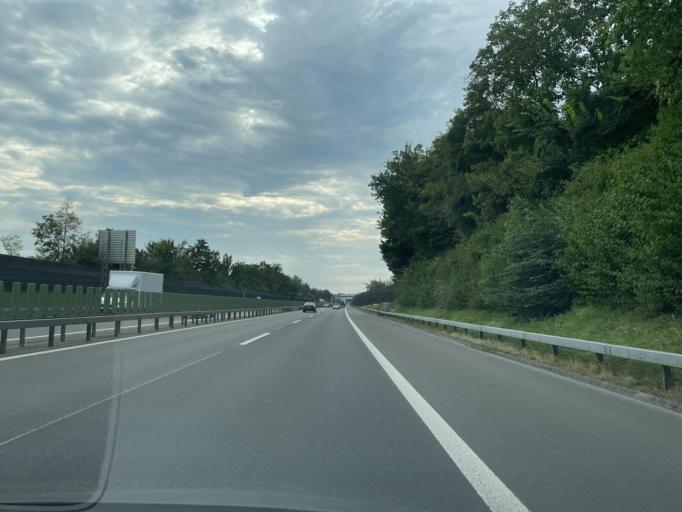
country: CH
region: Zug
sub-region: Zug
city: Steinhausen
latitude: 47.1907
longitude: 8.4975
